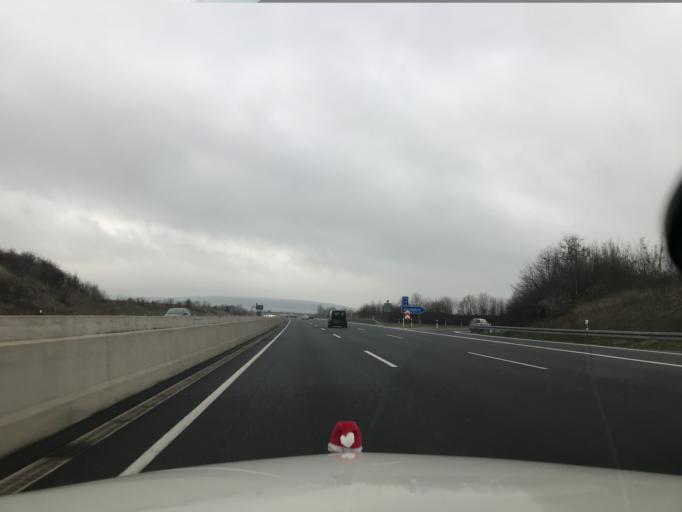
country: DE
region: Lower Saxony
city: Bockenem
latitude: 51.9993
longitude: 10.1566
